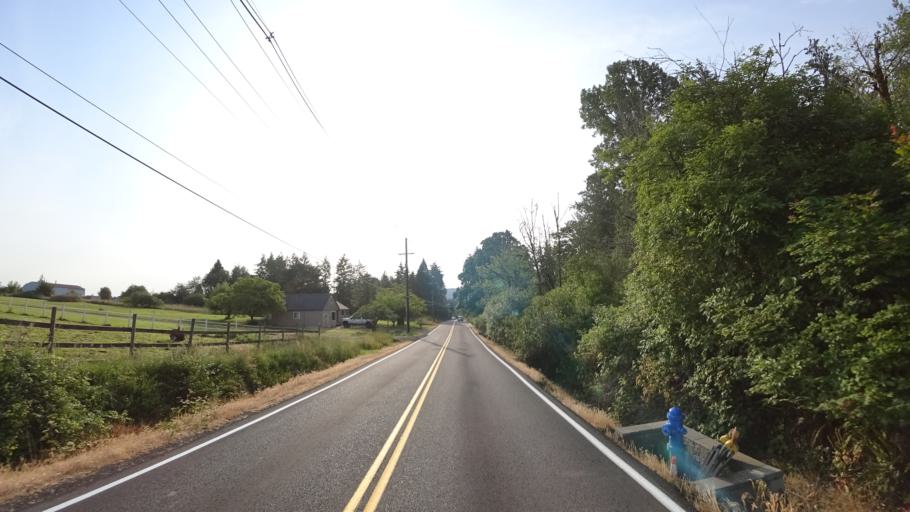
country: US
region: Oregon
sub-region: Clackamas County
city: Happy Valley
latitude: 45.4611
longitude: -122.5010
